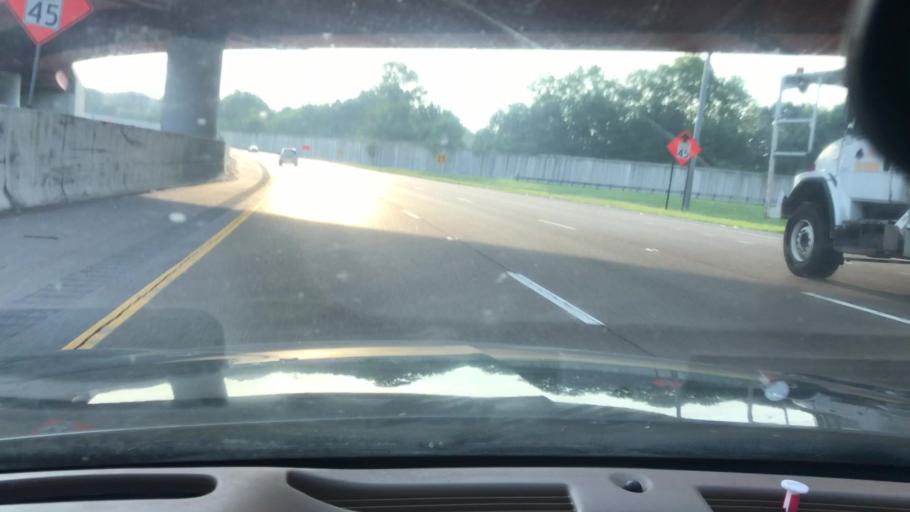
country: US
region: Tennessee
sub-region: Shelby County
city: Germantown
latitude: 35.0845
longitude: -89.8775
